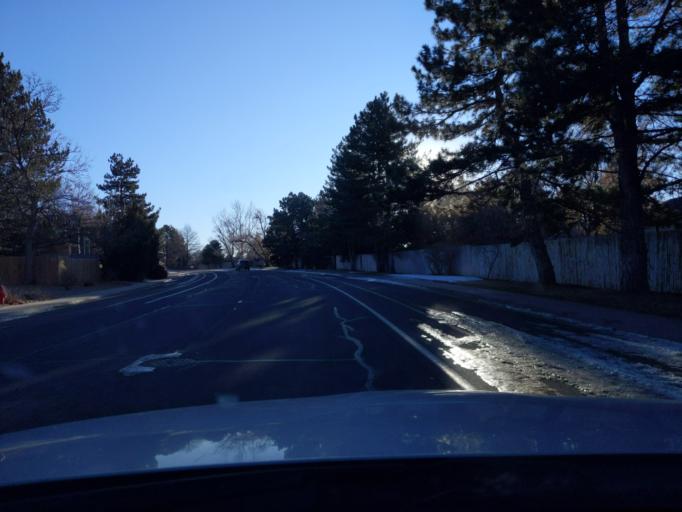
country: US
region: Colorado
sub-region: Arapahoe County
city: Centennial
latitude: 39.5700
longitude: -104.8889
